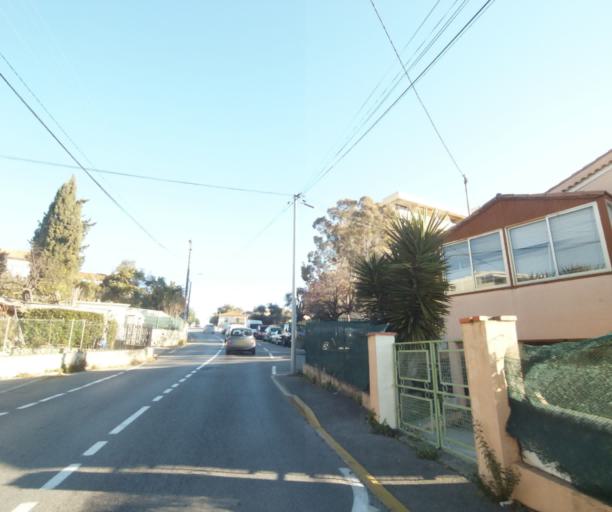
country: FR
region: Provence-Alpes-Cote d'Azur
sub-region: Departement des Alpes-Maritimes
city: Antibes
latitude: 43.5814
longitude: 7.1054
